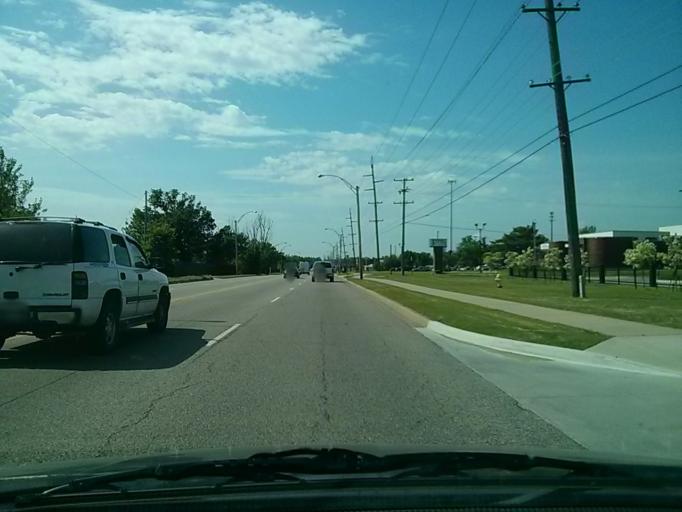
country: US
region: Oklahoma
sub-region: Tulsa County
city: Turley
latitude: 36.2103
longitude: -95.9757
